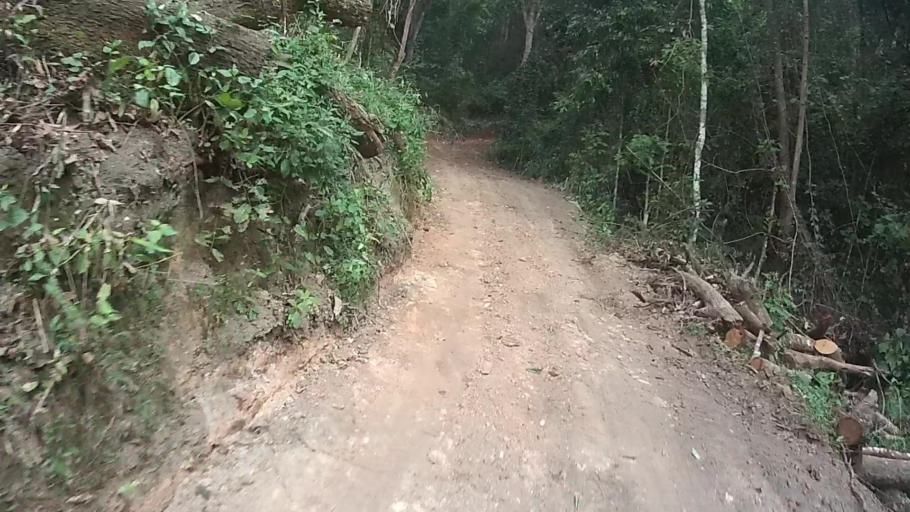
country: TH
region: Chiang Mai
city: Mae On
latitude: 18.7995
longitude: 99.3558
